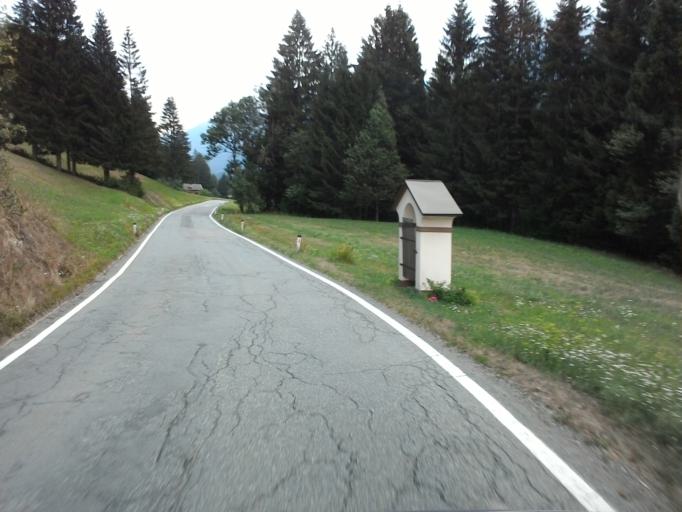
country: AT
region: Carinthia
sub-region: Politischer Bezirk Spittal an der Drau
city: Oberdrauburg
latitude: 46.6744
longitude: 12.9660
